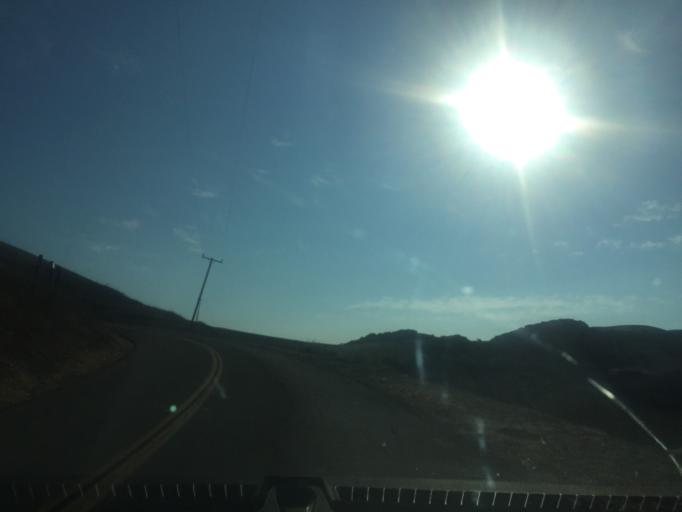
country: US
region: California
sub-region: Santa Barbara County
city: Lompoc
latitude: 34.5142
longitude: -120.4677
